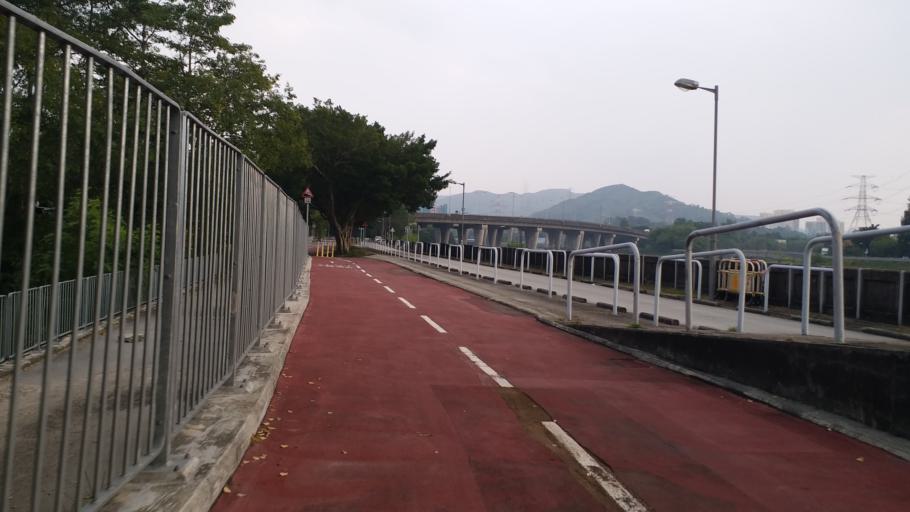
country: HK
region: Yuen Long
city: Yuen Long Kau Hui
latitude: 22.4559
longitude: 114.0484
